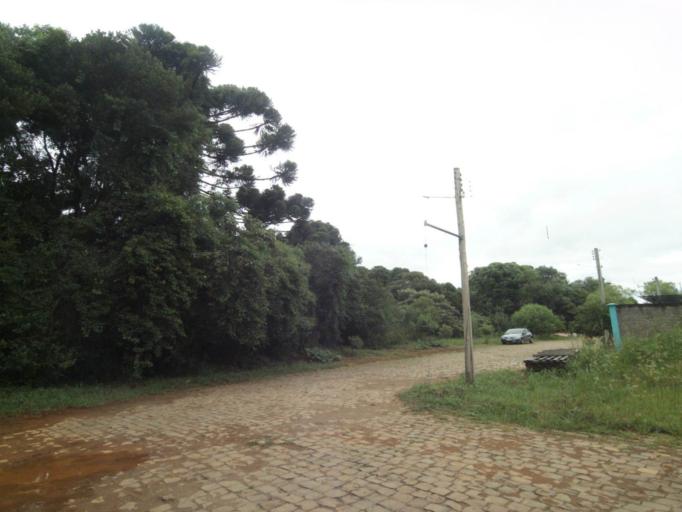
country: BR
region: Rio Grande do Sul
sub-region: Lagoa Vermelha
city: Lagoa Vermelha
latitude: -28.2159
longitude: -51.5293
